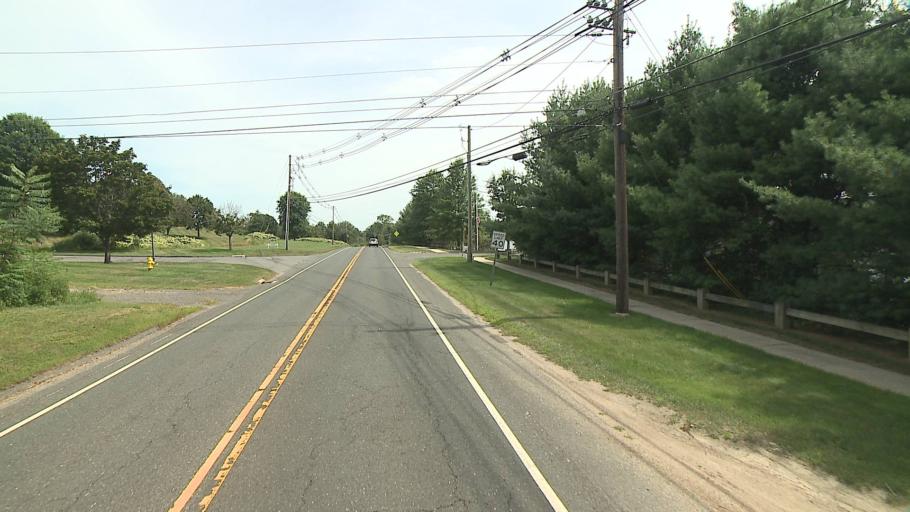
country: US
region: Connecticut
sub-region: Litchfield County
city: Oakville
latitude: 41.6132
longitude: -73.0961
